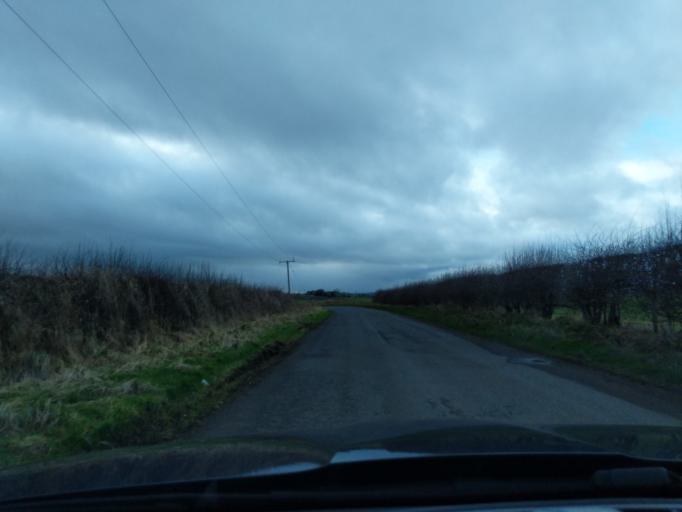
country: GB
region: England
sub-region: Northumberland
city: Ancroft
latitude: 55.7132
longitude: -2.0748
